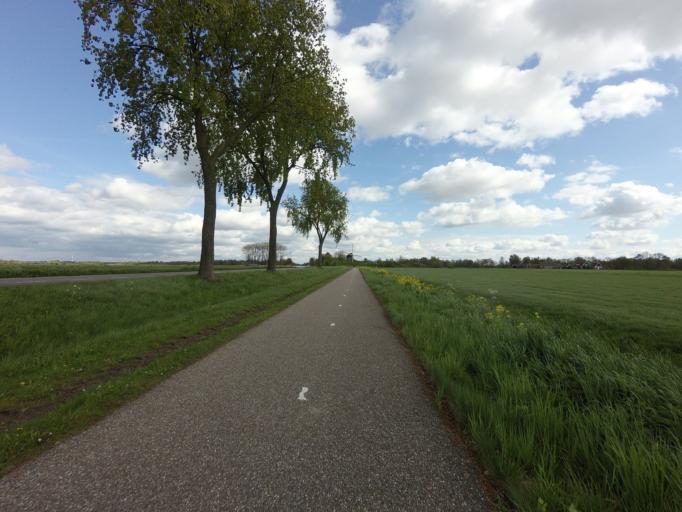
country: NL
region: Utrecht
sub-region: Stichtse Vecht
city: Vreeland
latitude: 52.2386
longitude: 5.0539
